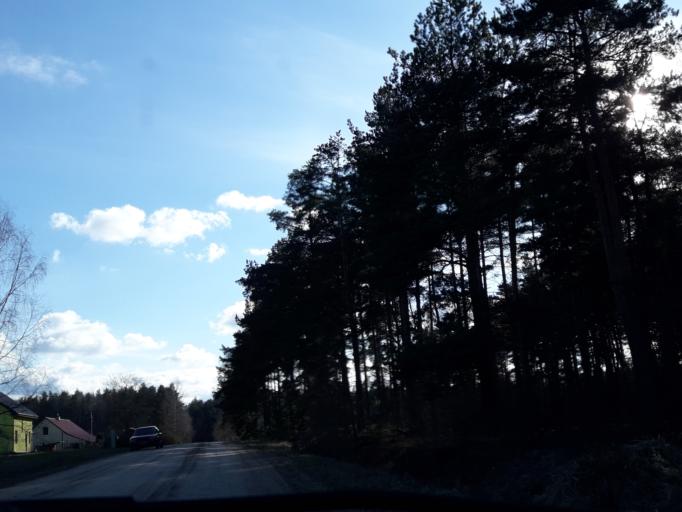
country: LV
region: Kekava
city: Kekava
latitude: 56.8521
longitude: 24.1870
